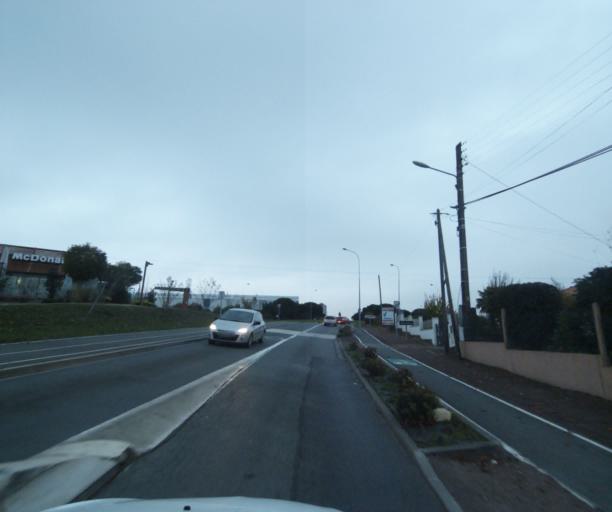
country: FR
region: Poitou-Charentes
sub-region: Departement de la Charente-Maritime
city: Fontcouverte
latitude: 45.7461
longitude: -0.6023
